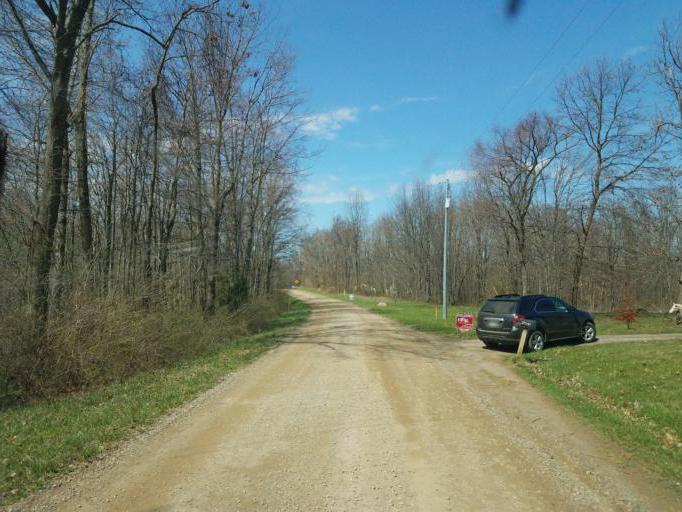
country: US
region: Ohio
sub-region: Knox County
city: Oak Hill
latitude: 40.3629
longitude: -82.2224
